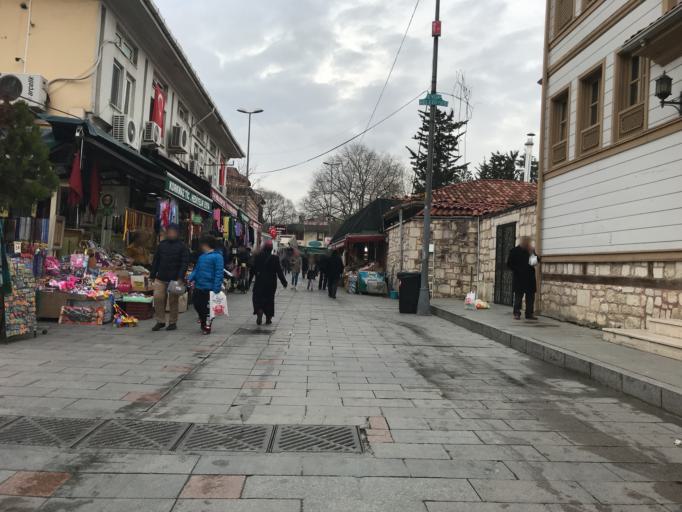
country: TR
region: Istanbul
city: Istanbul
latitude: 41.0464
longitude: 28.9341
